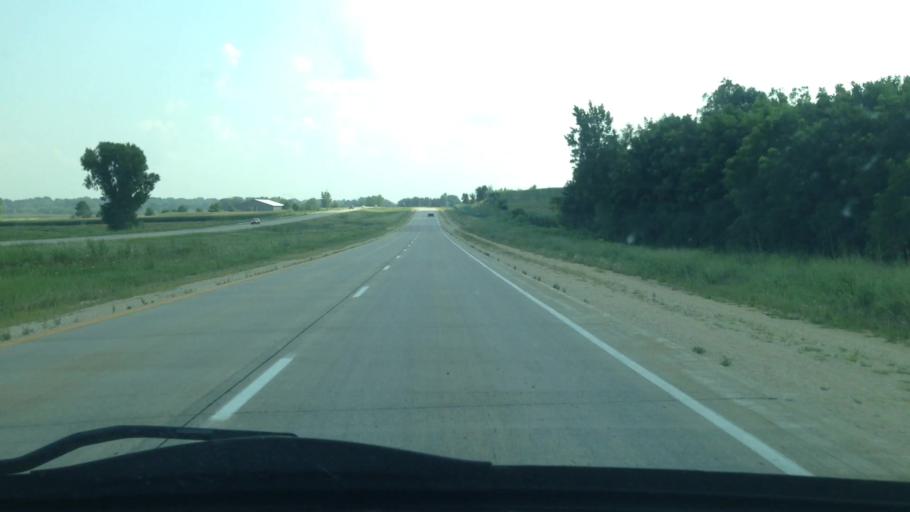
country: US
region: Iowa
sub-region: Bremer County
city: Denver
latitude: 42.6912
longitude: -92.3377
